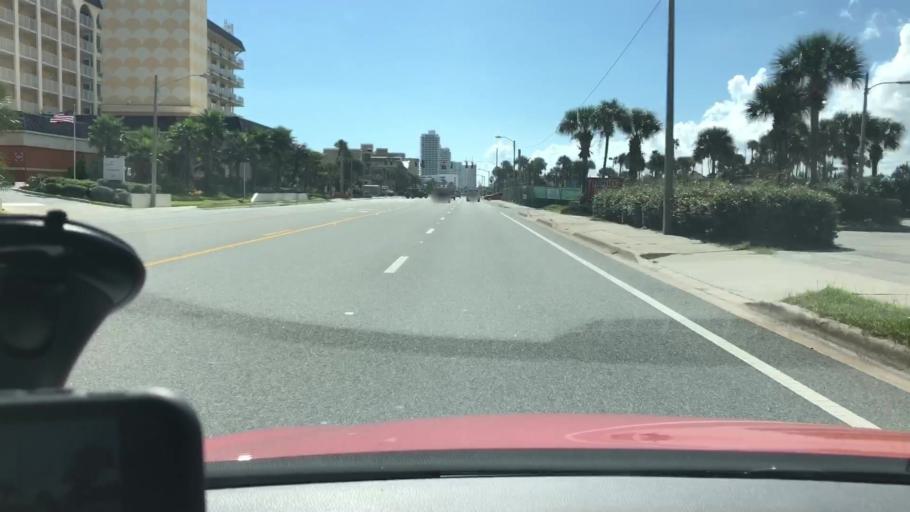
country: US
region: Florida
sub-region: Volusia County
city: Ormond Beach
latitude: 29.2765
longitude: -81.0324
